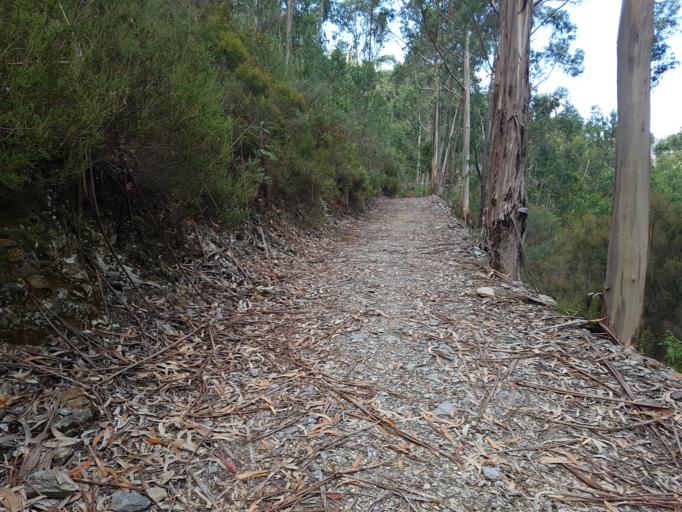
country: PT
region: Coimbra
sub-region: Oliveira do Hospital
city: Oliveira do Hospital
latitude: 40.2412
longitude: -7.8075
